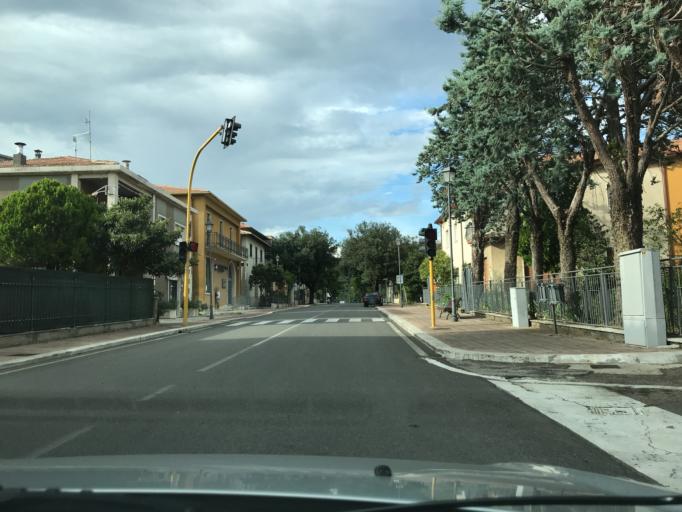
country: IT
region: Umbria
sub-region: Provincia di Terni
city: Guardea
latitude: 42.6251
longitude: 12.2960
